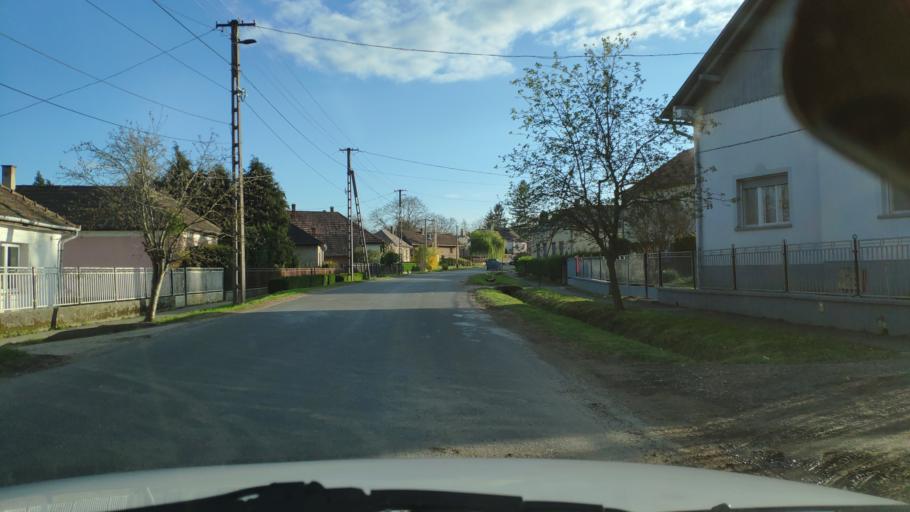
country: HU
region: Zala
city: Zalakomar
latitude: 46.4504
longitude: 17.1242
